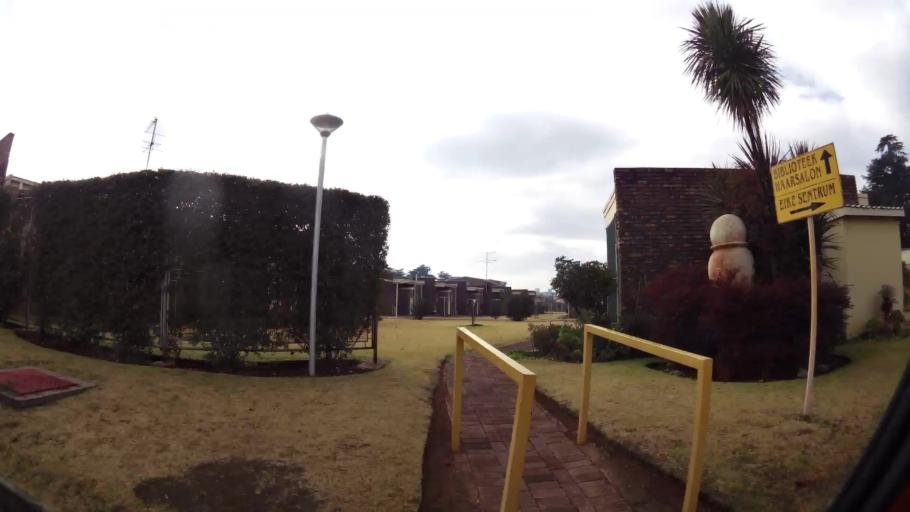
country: ZA
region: Gauteng
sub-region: Sedibeng District Municipality
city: Vanderbijlpark
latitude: -26.7052
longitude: 27.8314
